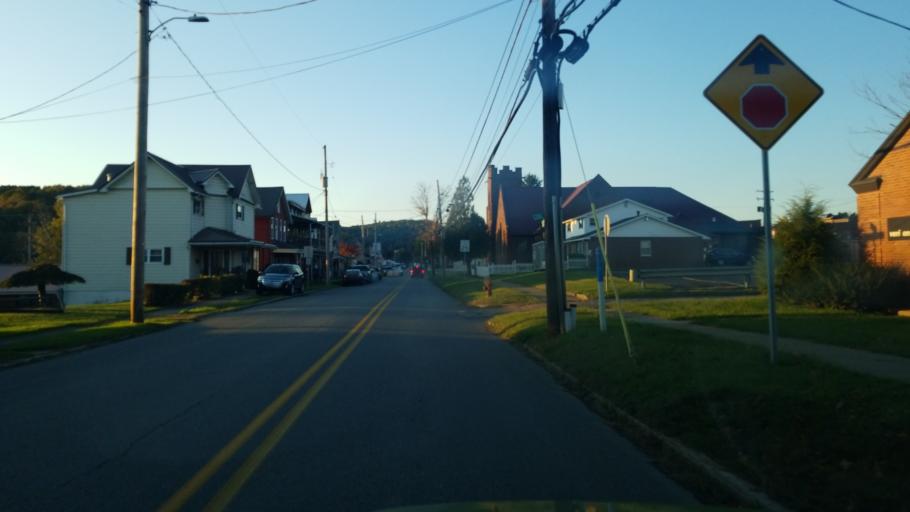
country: US
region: Pennsylvania
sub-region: Jefferson County
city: Reynoldsville
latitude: 41.0939
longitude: -78.8882
